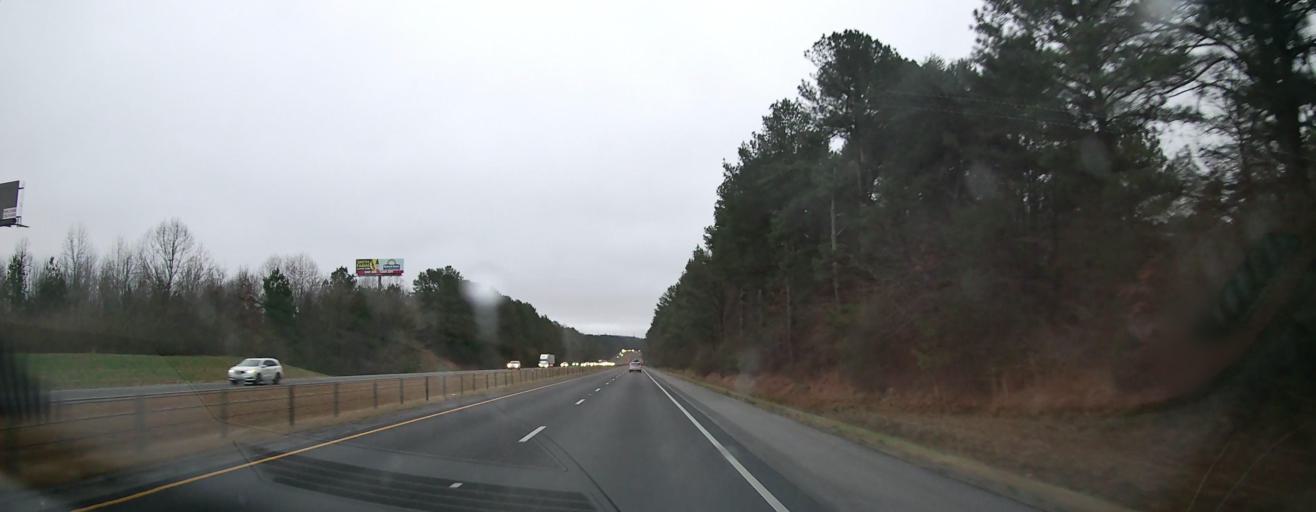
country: US
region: Alabama
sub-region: Cullman County
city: Cullman
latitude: 34.2385
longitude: -86.8824
